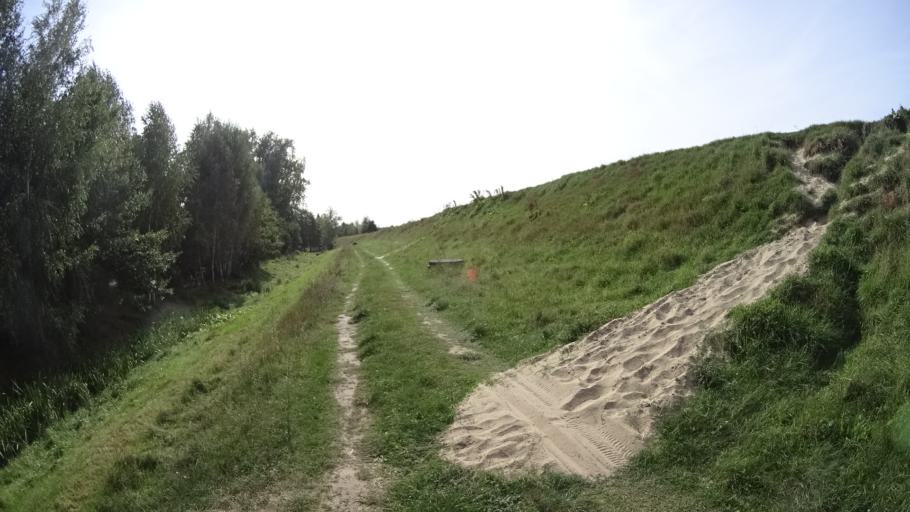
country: PL
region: Masovian Voivodeship
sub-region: Powiat legionowski
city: Serock
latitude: 52.5015
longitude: 21.0840
